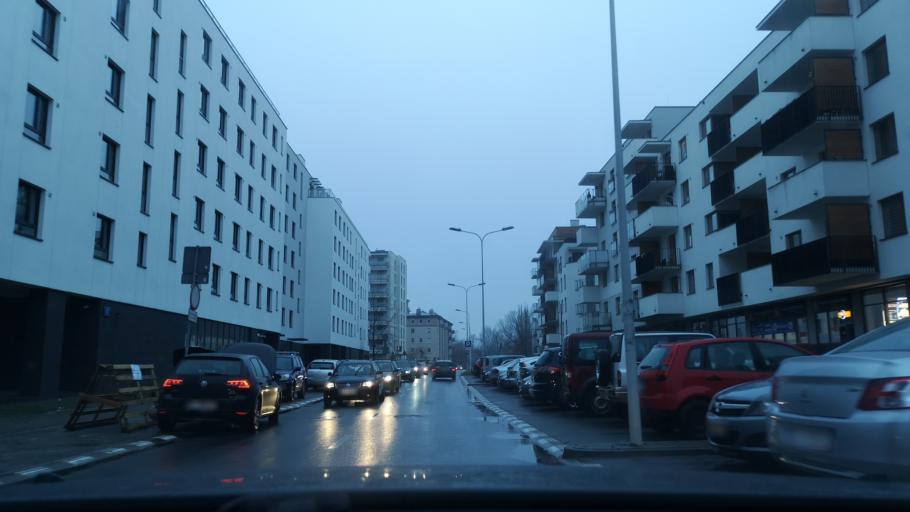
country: PL
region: Masovian Voivodeship
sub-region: Warszawa
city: Bemowo
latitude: 52.2419
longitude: 20.9091
